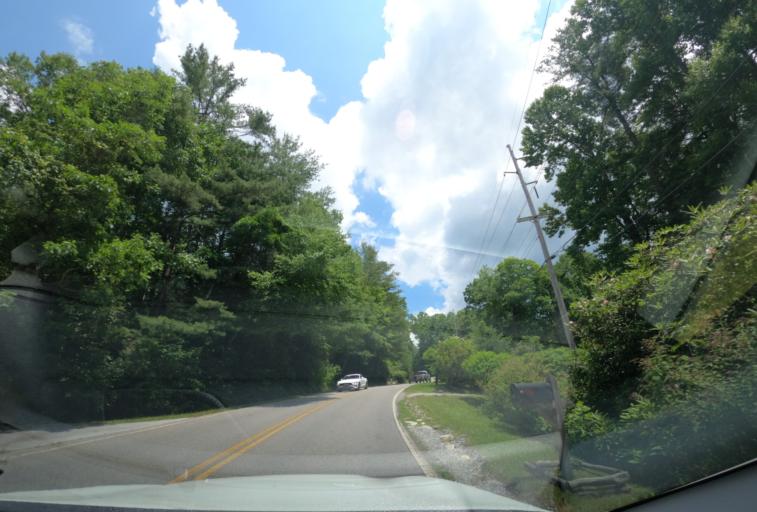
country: US
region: North Carolina
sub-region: Macon County
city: Franklin
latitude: 35.0745
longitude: -83.1939
